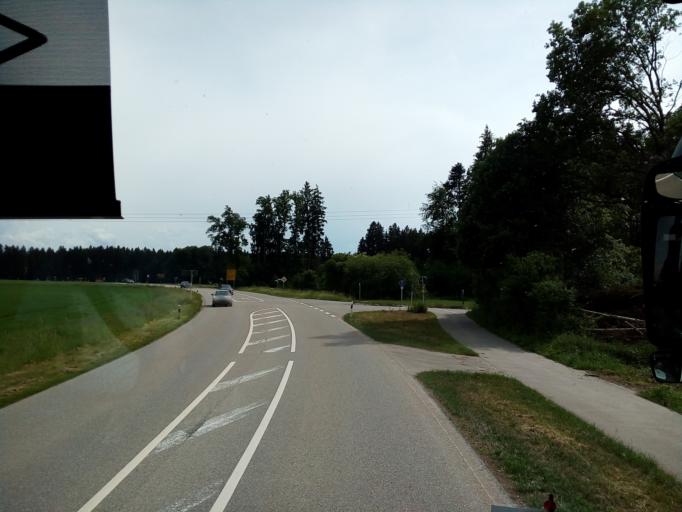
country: DE
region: Bavaria
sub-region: Upper Bavaria
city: Obing
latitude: 47.9930
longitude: 12.4186
